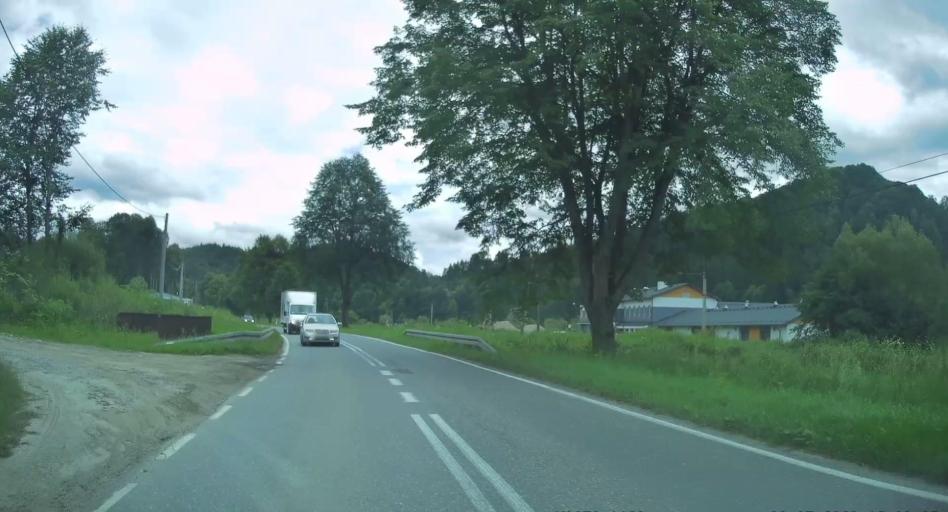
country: PL
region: Lesser Poland Voivodeship
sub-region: Powiat nowosadecki
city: Muszyna
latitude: 49.3442
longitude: 20.8719
